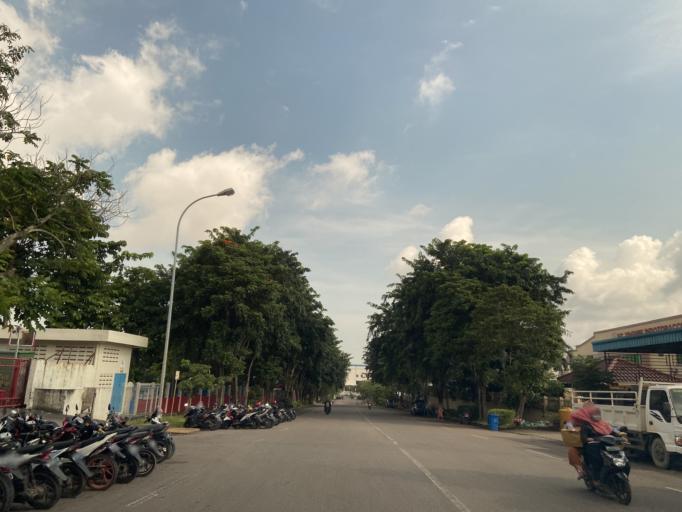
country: SG
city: Singapore
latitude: 1.1082
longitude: 104.0722
